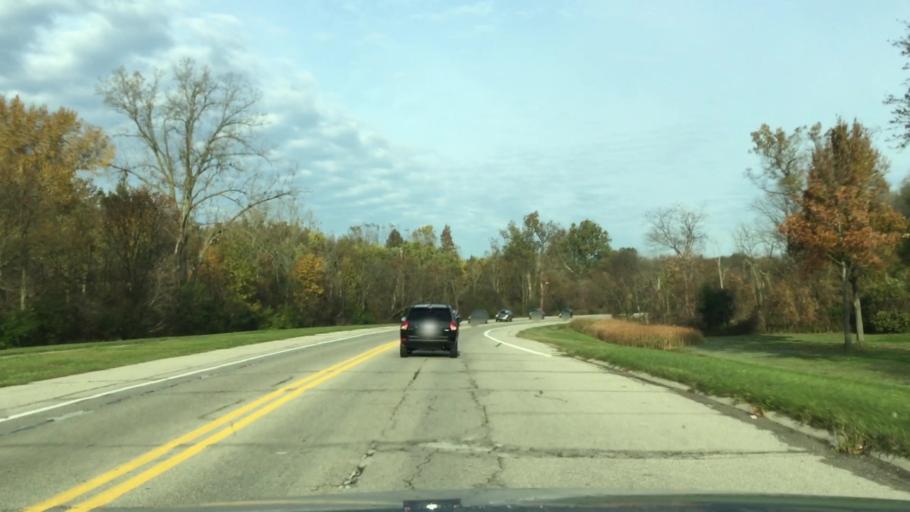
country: US
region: Michigan
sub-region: Wayne County
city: Dearborn Heights
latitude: 42.3331
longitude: -83.2557
